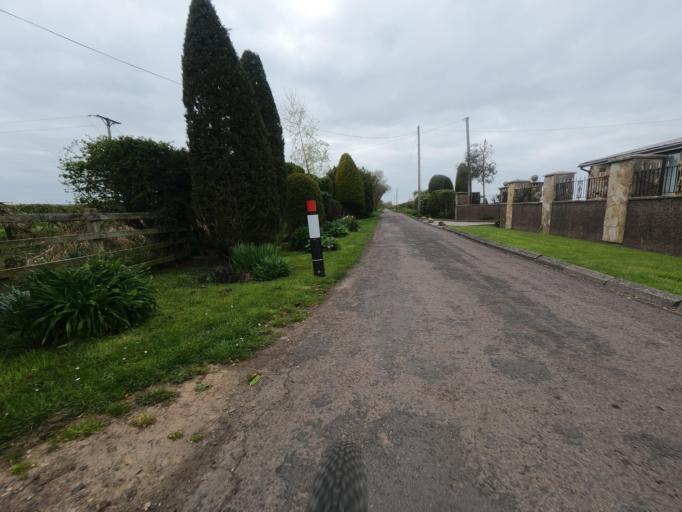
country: GB
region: England
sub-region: Northumberland
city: Ponteland
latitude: 55.0564
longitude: -1.7116
